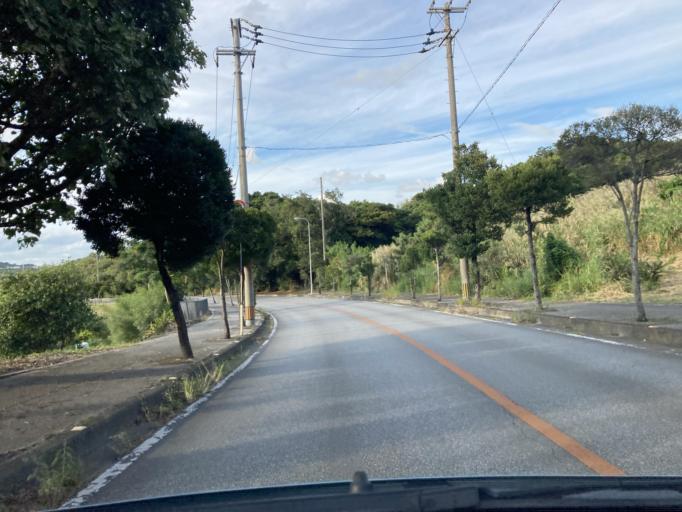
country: JP
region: Okinawa
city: Itoman
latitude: 26.1335
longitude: 127.7226
